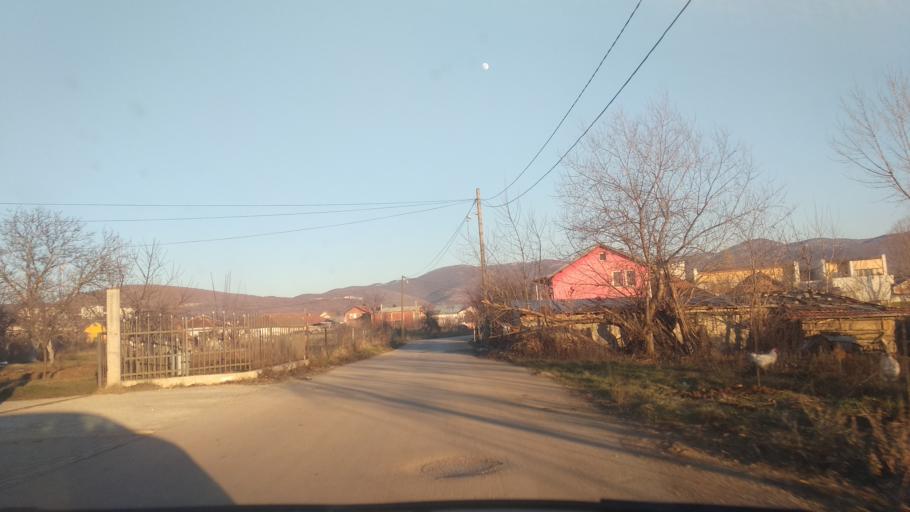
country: XK
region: Pristina
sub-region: Komuna e Prishtines
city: Pristina
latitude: 42.6007
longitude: 21.1850
